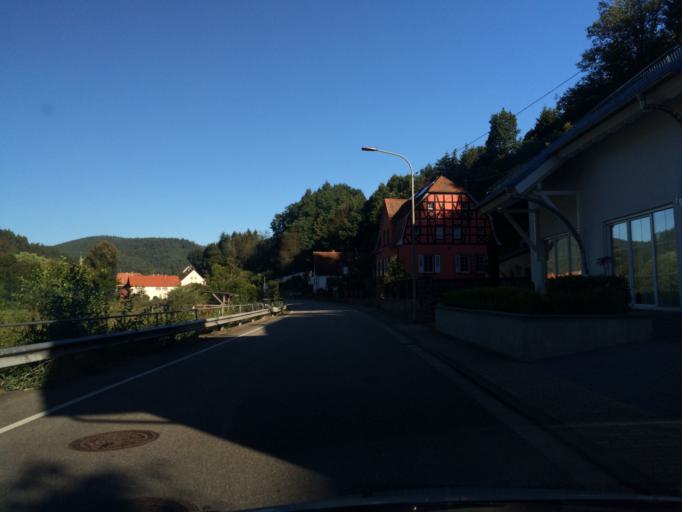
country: DE
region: Rheinland-Pfalz
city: Bobenthal
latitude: 49.0616
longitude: 7.8615
